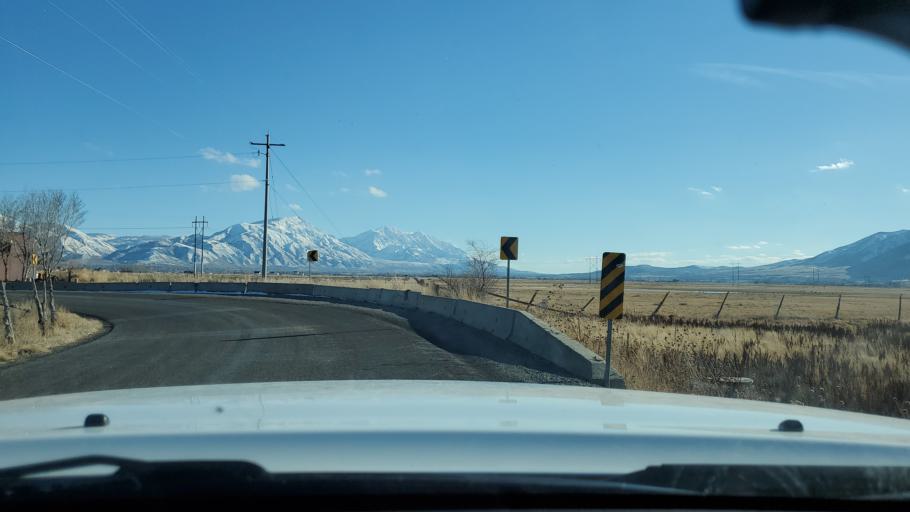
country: US
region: Utah
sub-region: Utah County
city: Benjamin
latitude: 40.1144
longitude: -111.7691
